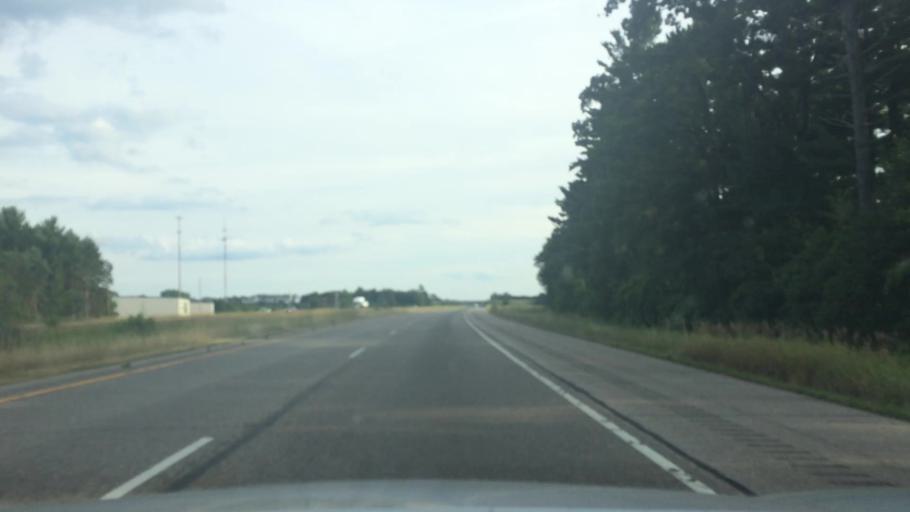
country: US
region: Wisconsin
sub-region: Waushara County
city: Wautoma
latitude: 44.1931
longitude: -89.5238
